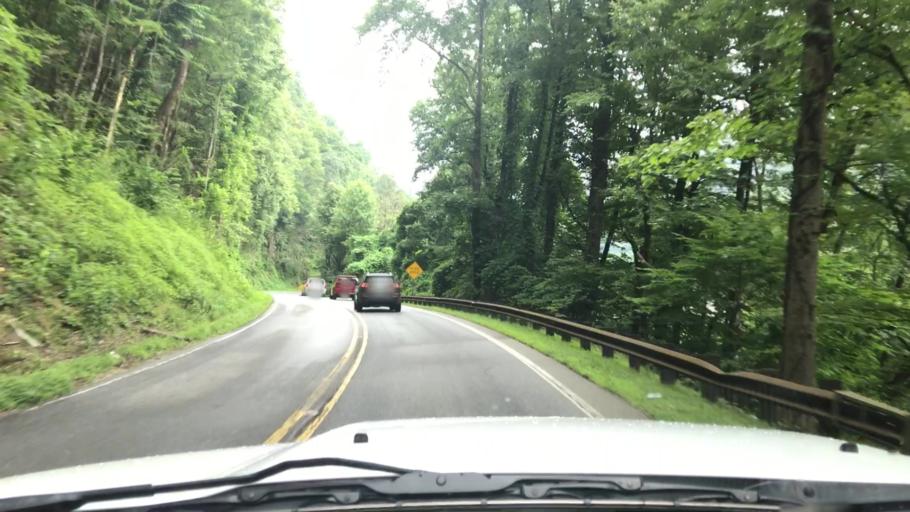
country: US
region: North Carolina
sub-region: Graham County
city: Robbinsville
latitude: 35.3101
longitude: -83.6435
